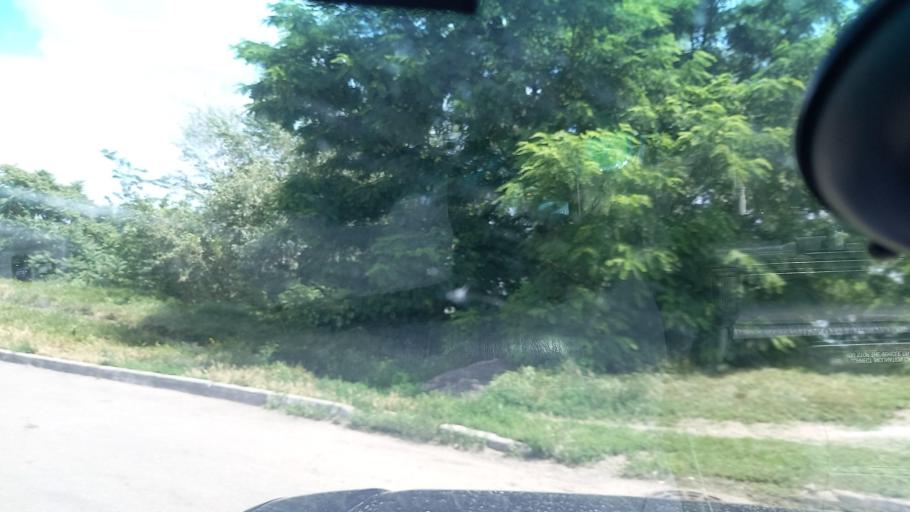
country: RU
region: Krasnodarskiy
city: Krasnodar
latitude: 45.0364
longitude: 38.9345
